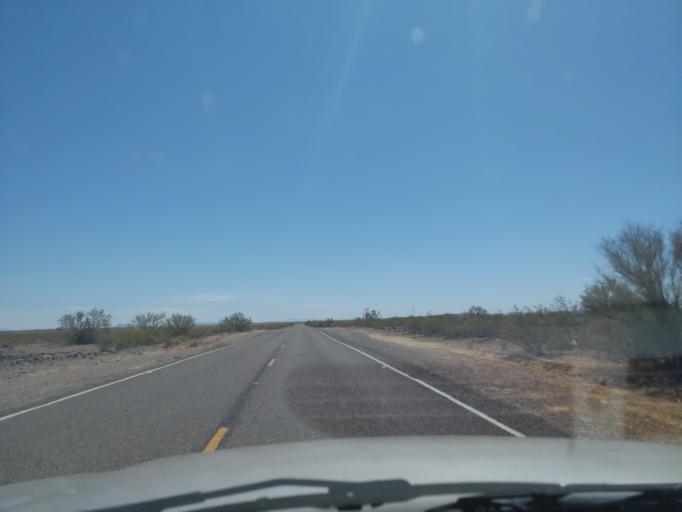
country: US
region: Arizona
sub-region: Maricopa County
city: Gila Bend
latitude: 32.8833
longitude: -113.2303
